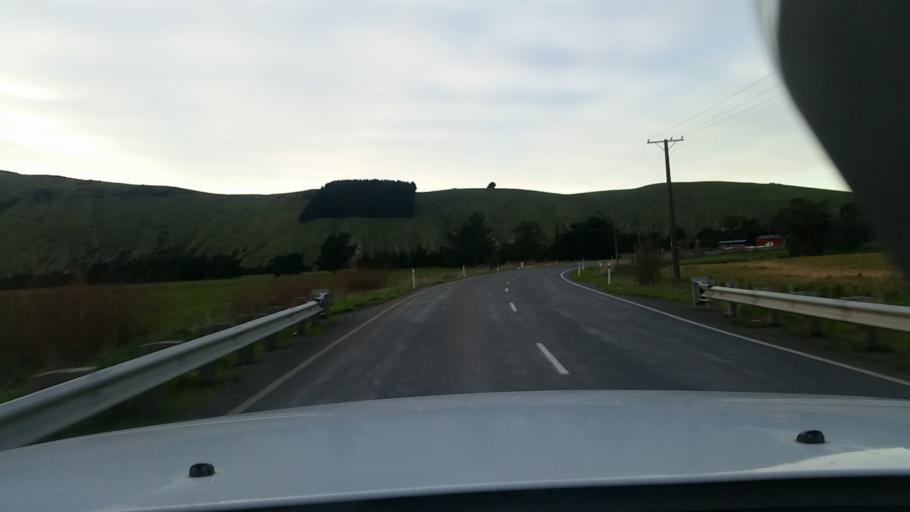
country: NZ
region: Canterbury
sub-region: Selwyn District
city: Lincoln
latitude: -43.7309
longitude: 172.6121
